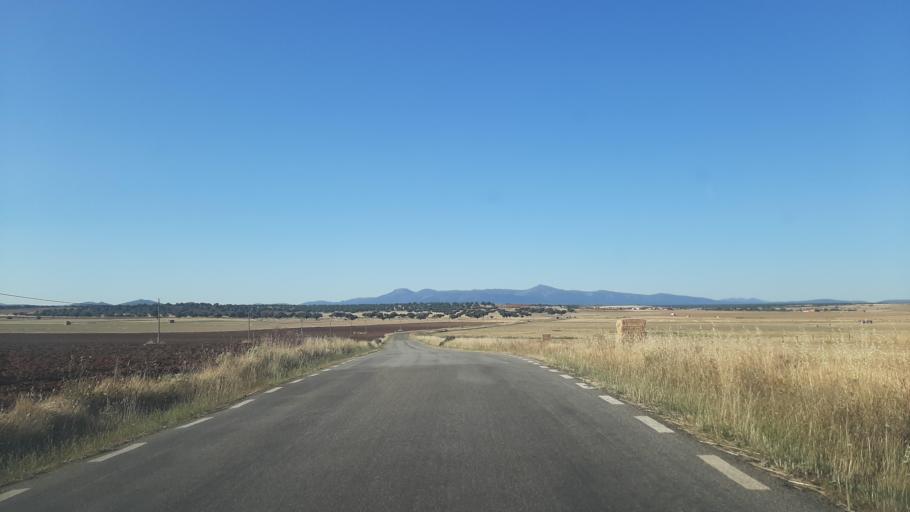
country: ES
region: Castille and Leon
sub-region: Provincia de Salamanca
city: Cabrillas
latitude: 40.7241
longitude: -6.1762
